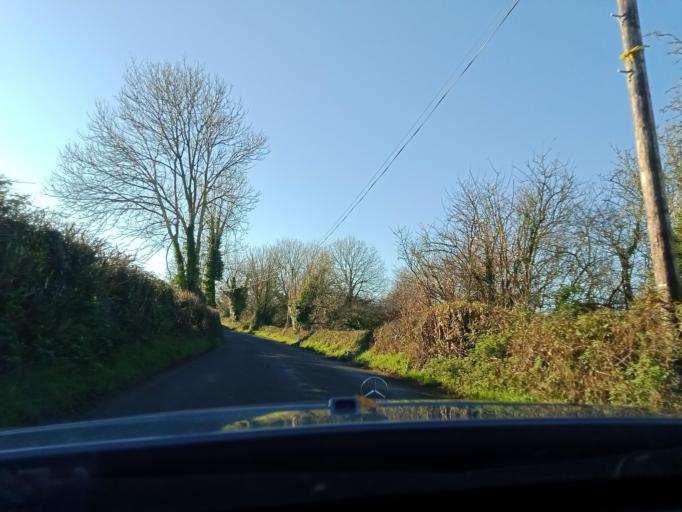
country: IE
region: Leinster
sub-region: Kilkenny
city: Mooncoin
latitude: 52.2919
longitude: -7.2283
